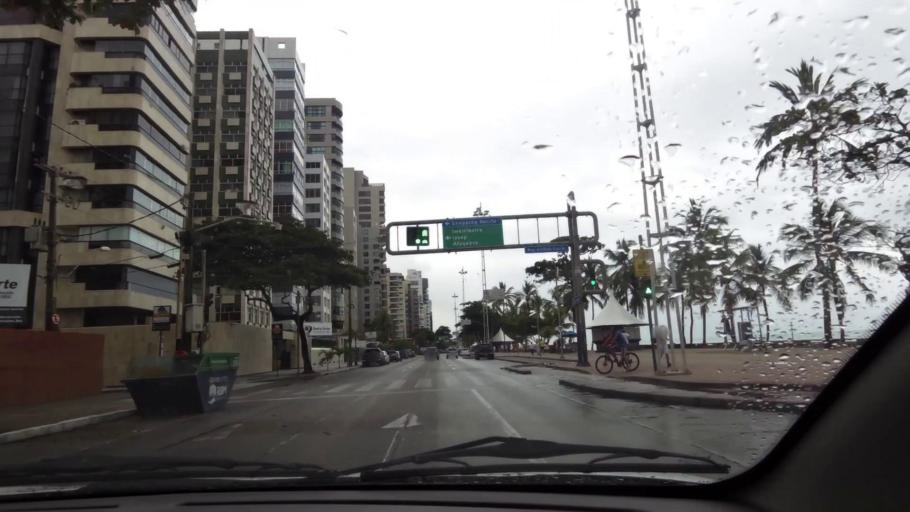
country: BR
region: Pernambuco
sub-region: Recife
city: Recife
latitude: -8.1171
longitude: -34.8932
